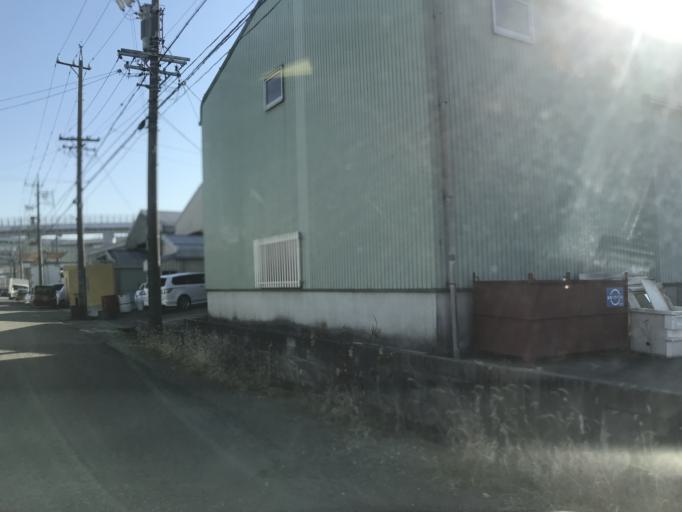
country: JP
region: Aichi
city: Iwakura
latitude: 35.2221
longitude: 136.8514
